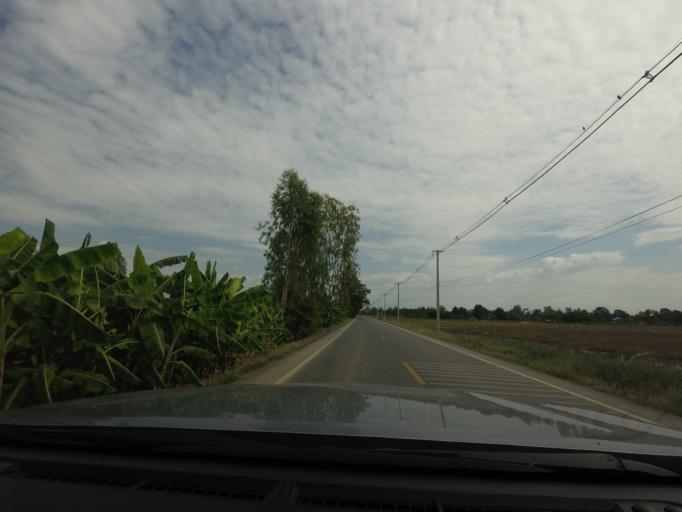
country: TH
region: Phitsanulok
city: Wang Thong
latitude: 16.7223
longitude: 100.3477
